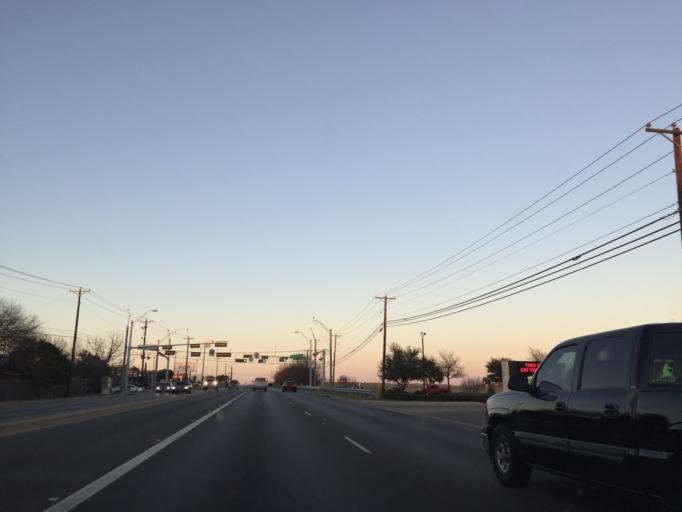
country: US
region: Texas
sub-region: Travis County
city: Pflugerville
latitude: 30.4450
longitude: -97.6085
